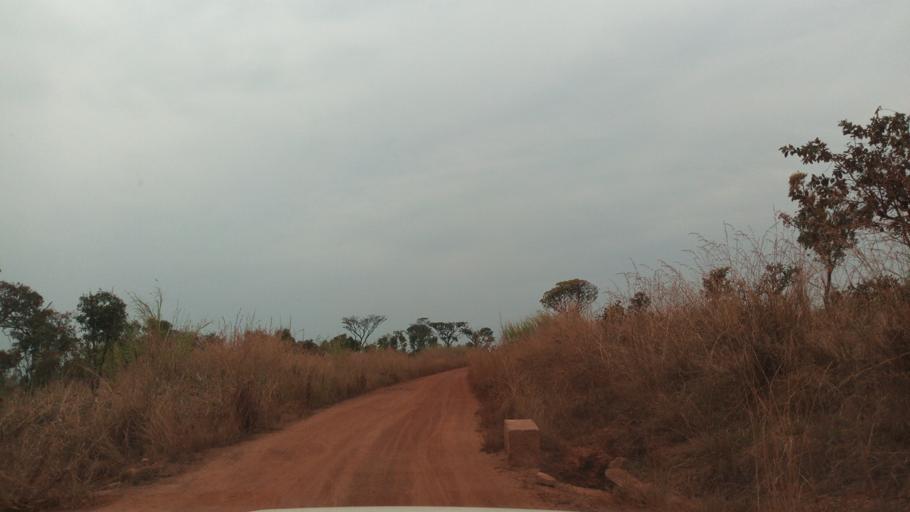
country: ZM
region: Northern
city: Kaputa
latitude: -7.7136
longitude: 29.2562
